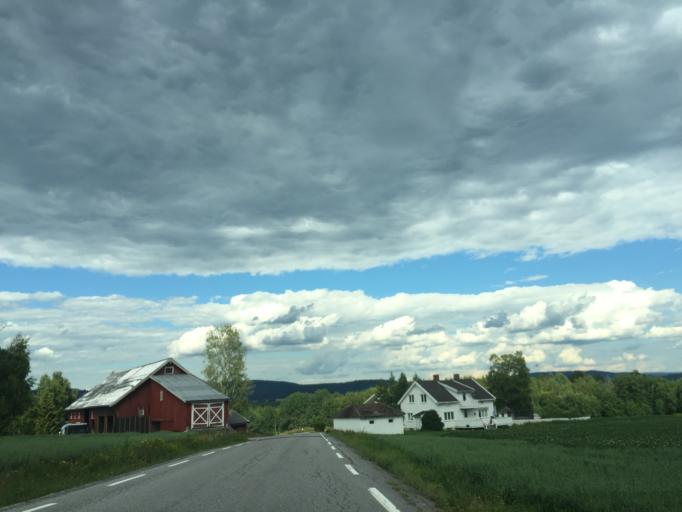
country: NO
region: Hedmark
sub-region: Kongsvinger
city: Spetalen
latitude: 60.1971
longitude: 11.8365
